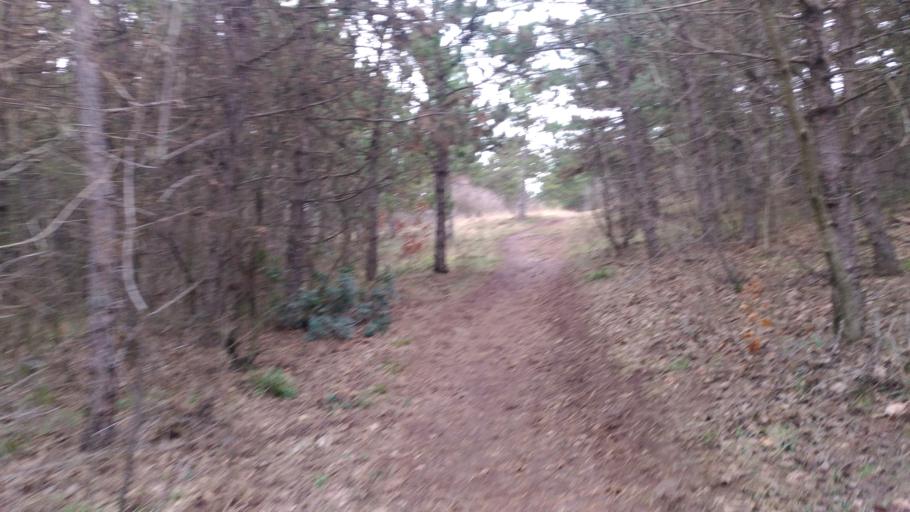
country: HU
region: Pest
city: Urom
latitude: 47.5877
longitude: 19.0185
